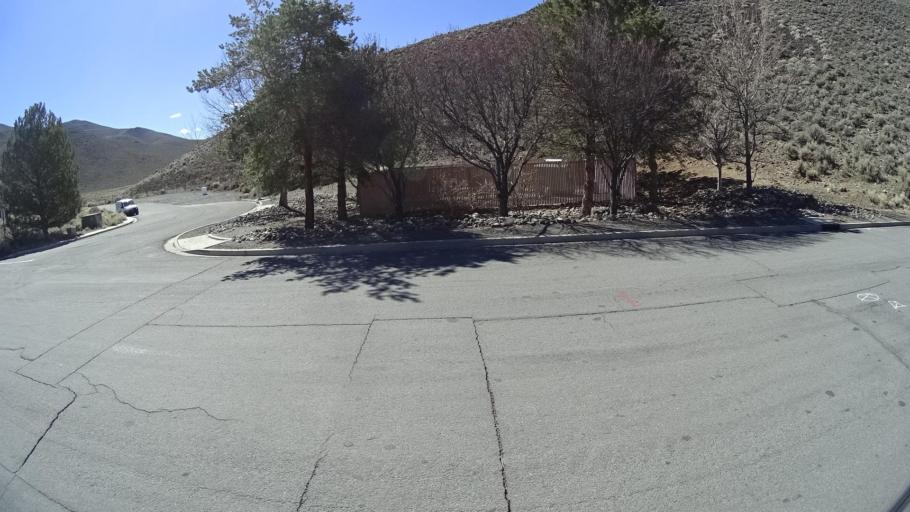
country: US
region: Nevada
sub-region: Washoe County
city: Sparks
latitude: 39.4768
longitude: -119.7236
